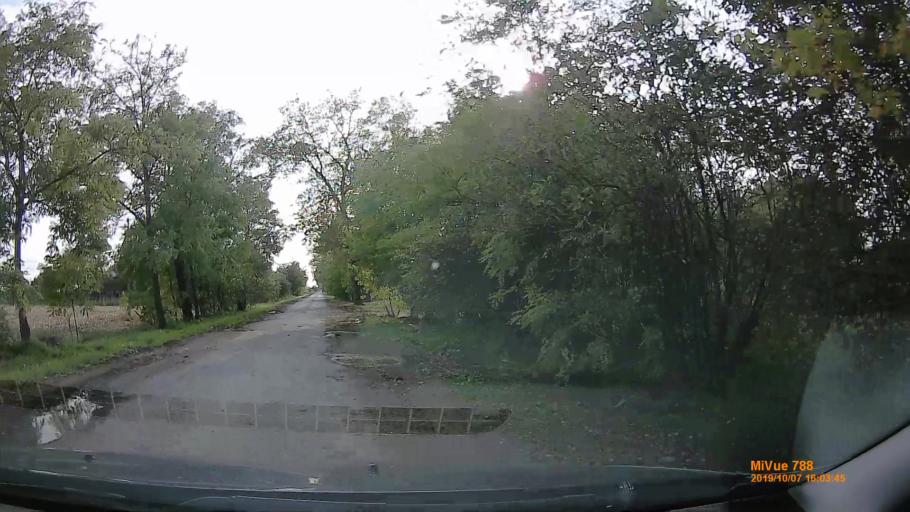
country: HU
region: Bekes
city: Szarvas
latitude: 46.8082
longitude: 20.6432
